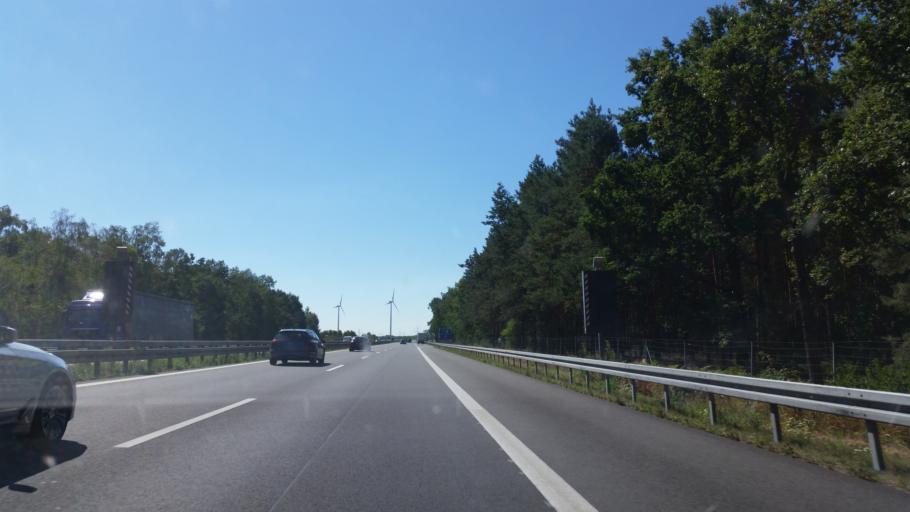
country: DE
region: Brandenburg
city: Kasel-Golzig
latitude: 51.9993
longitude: 13.7226
